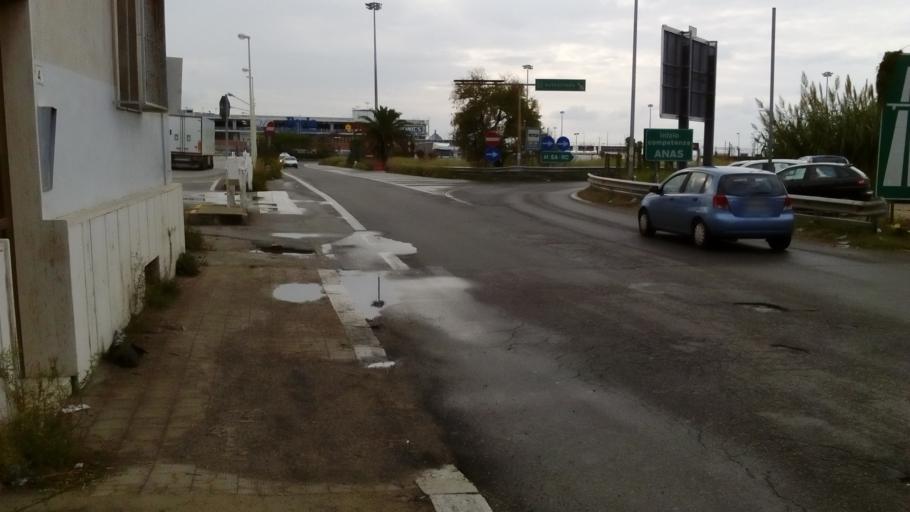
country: IT
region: Calabria
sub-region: Provincia di Reggio Calabria
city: Campo Calabro
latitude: 38.2164
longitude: 15.6364
